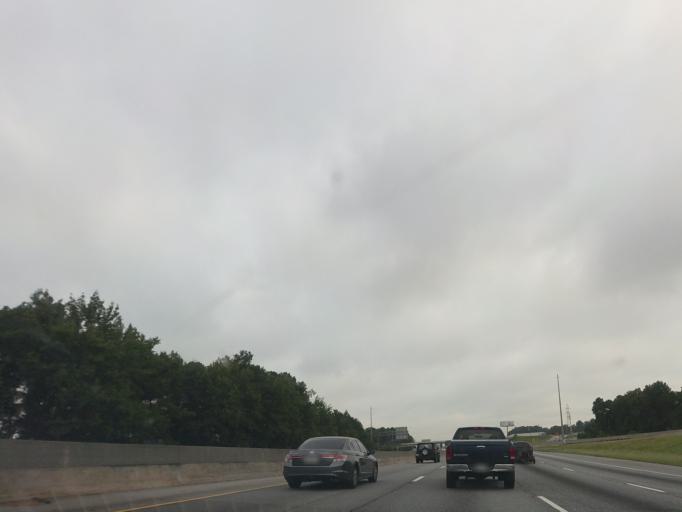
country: US
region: Georgia
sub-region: Clayton County
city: Riverdale
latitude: 33.5891
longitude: -84.3837
